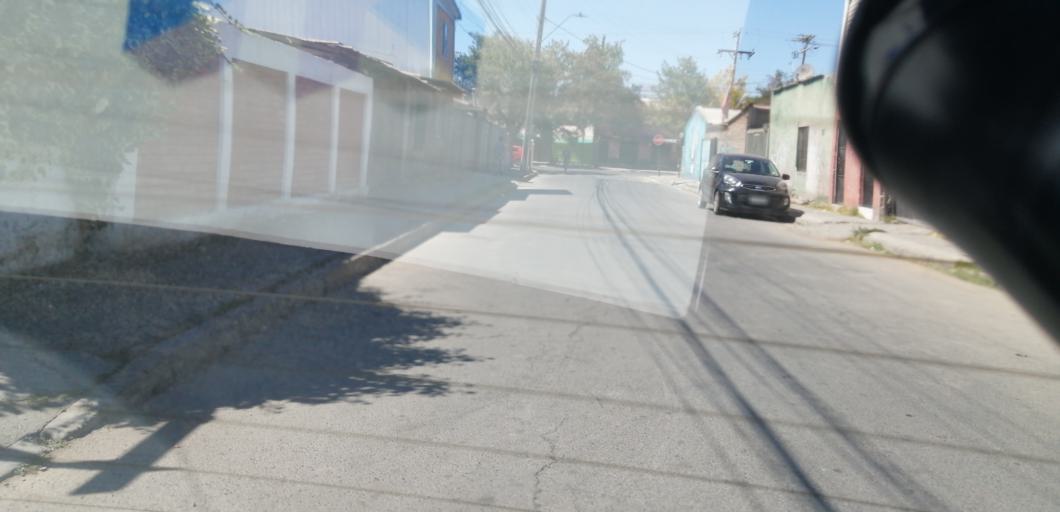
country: CL
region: Santiago Metropolitan
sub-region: Provincia de Santiago
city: Lo Prado
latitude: -33.4314
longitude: -70.7628
